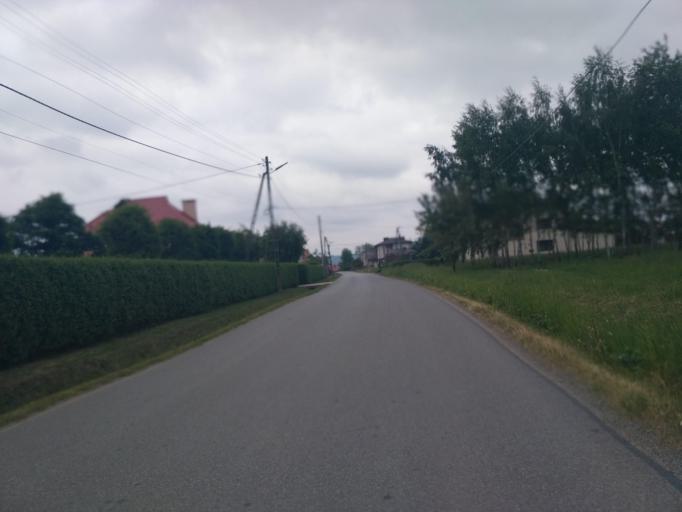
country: PL
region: Subcarpathian Voivodeship
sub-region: Krosno
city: Krosno
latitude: 49.6682
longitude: 21.7220
